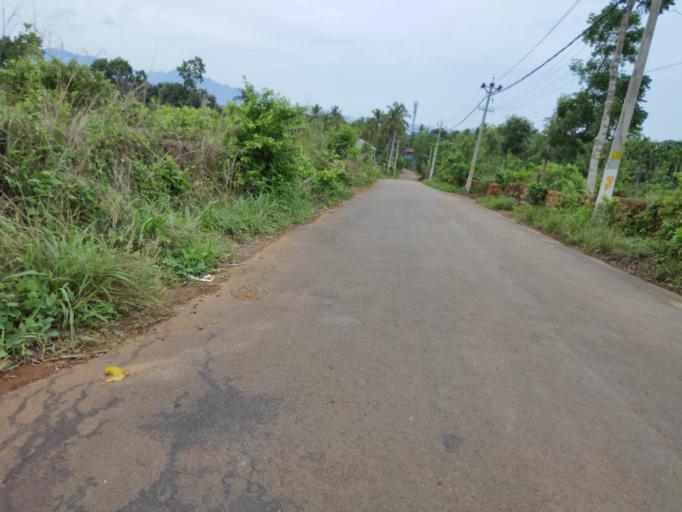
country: IN
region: Kerala
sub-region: Malappuram
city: Manjeri
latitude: 11.2483
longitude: 76.2475
